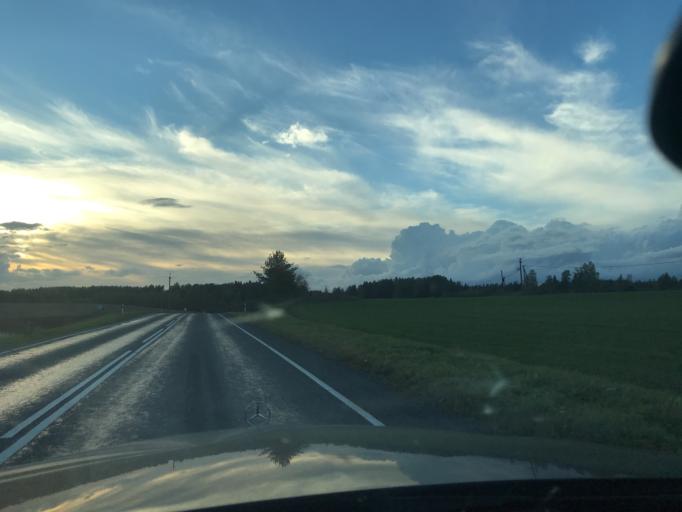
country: EE
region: Vorumaa
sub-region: Antsla vald
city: Vana-Antsla
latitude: 57.8696
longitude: 26.6030
